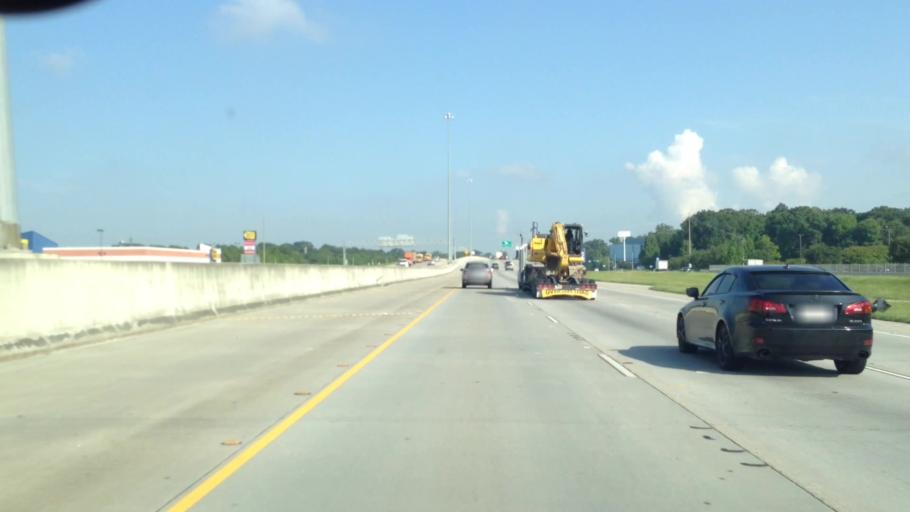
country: US
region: Louisiana
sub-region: East Baton Rouge Parish
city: Inniswold
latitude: 30.3921
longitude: -91.0811
